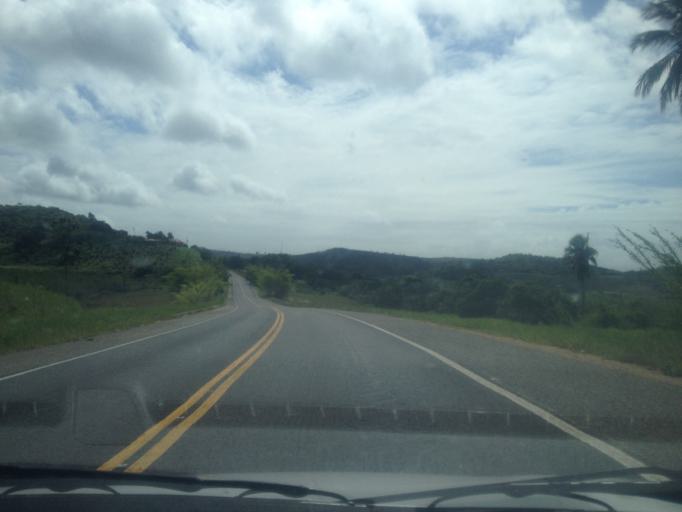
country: BR
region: Bahia
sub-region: Conde
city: Conde
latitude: -11.9601
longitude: -37.6698
